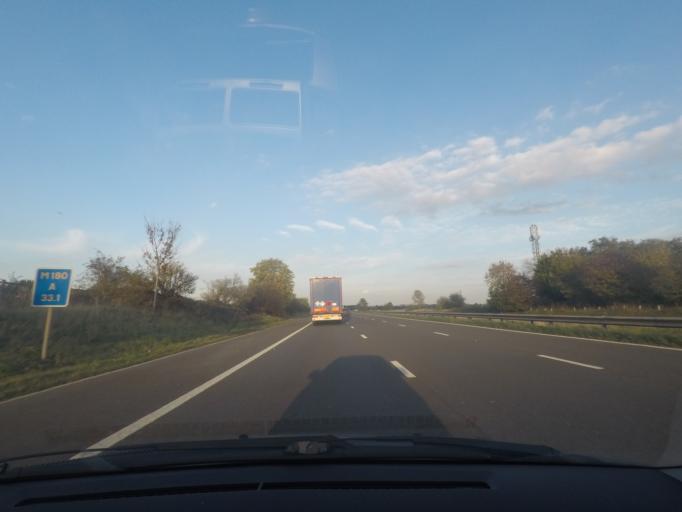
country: GB
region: England
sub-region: North Lincolnshire
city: Brigg
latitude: 53.5532
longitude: -0.5144
